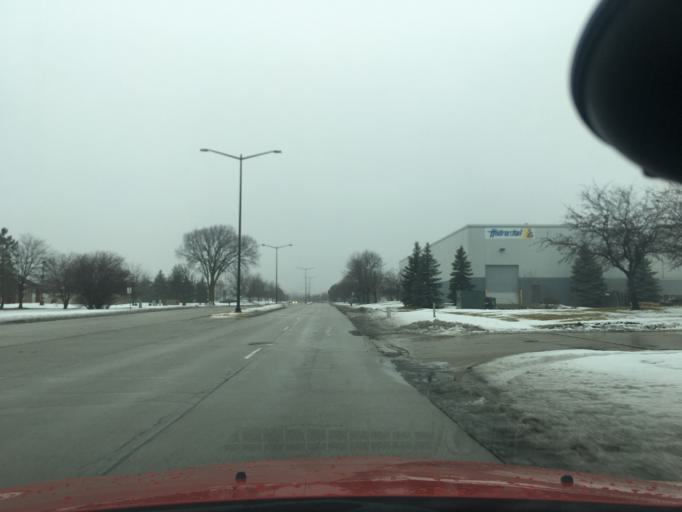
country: US
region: Illinois
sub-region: Kane County
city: North Aurora
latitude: 41.7953
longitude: -88.2577
